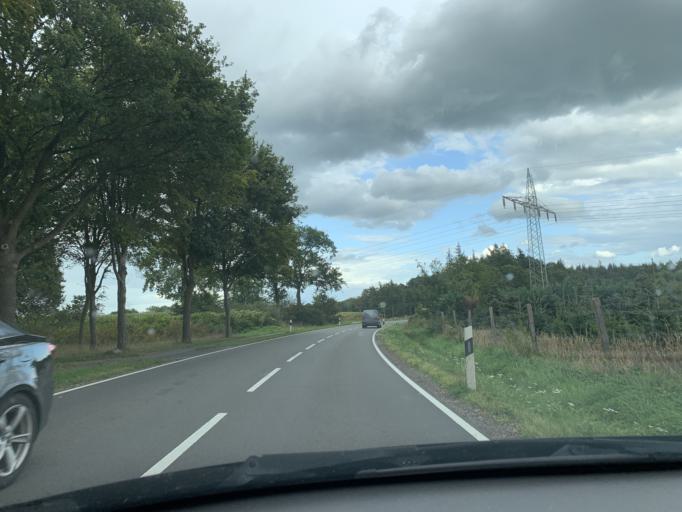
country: DE
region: Lower Saxony
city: Westerstede
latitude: 53.2855
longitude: 7.9889
